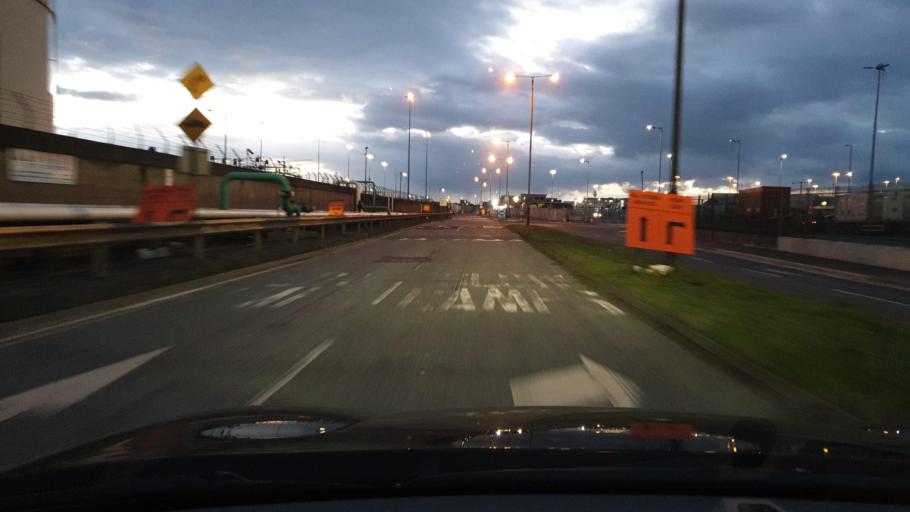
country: IE
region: Leinster
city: Ringsend
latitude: 53.3520
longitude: -6.2156
